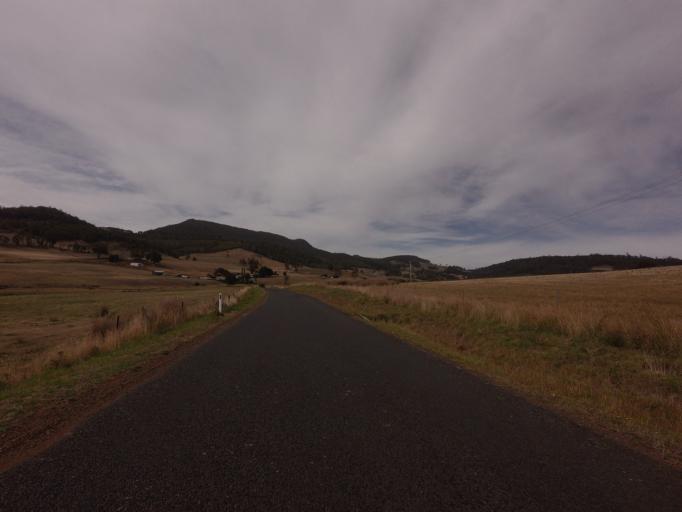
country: AU
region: Tasmania
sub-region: Sorell
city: Sorell
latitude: -42.4776
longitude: 147.5743
